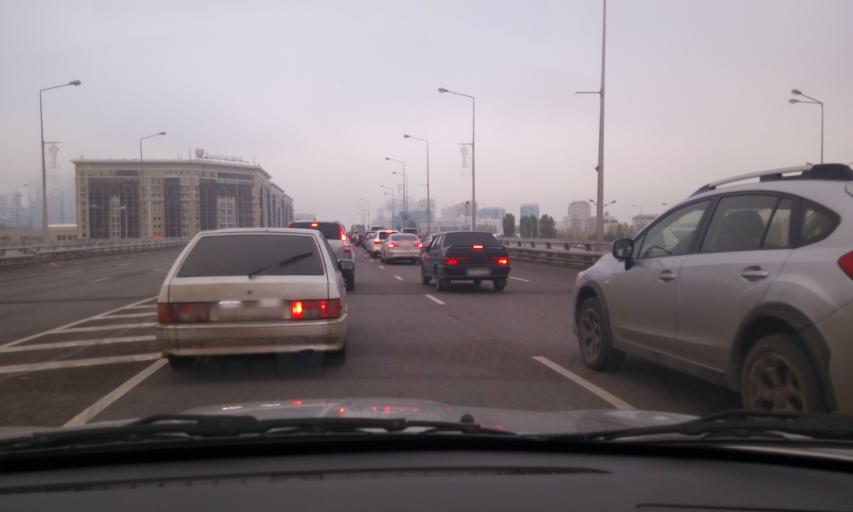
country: KZ
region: Astana Qalasy
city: Astana
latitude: 51.1319
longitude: 71.4431
